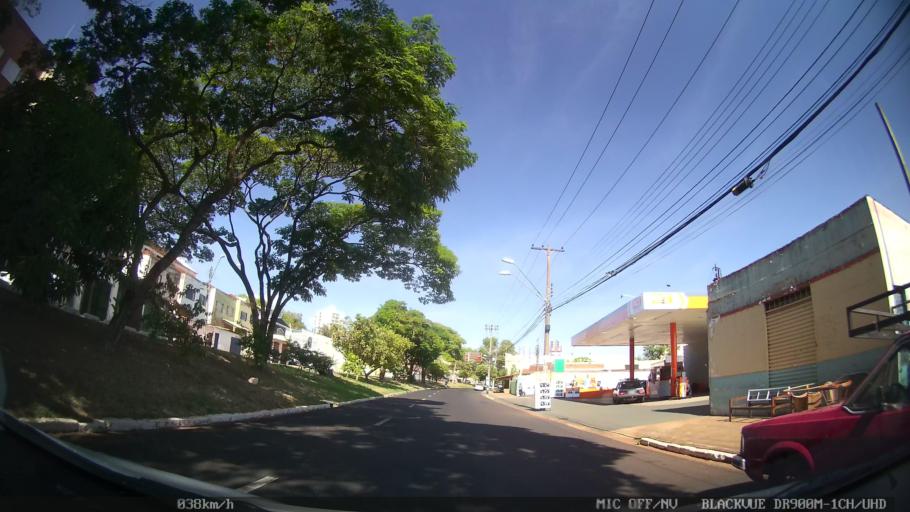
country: BR
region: Sao Paulo
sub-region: Ribeirao Preto
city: Ribeirao Preto
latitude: -21.1817
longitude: -47.8183
